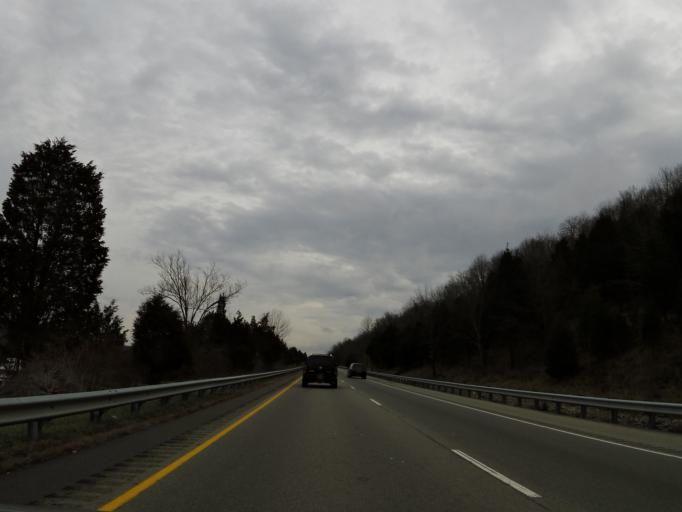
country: US
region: Indiana
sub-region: Dearborn County
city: Bright
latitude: 39.2751
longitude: -84.8969
